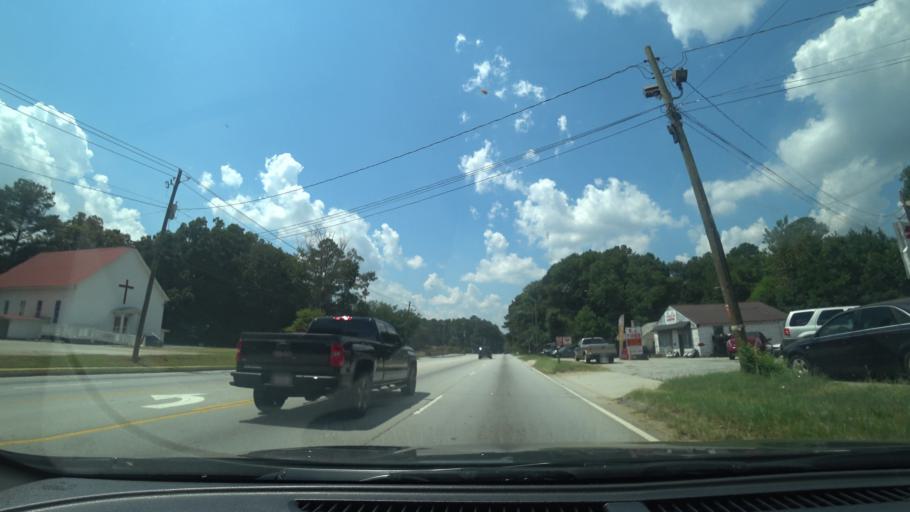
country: US
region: Georgia
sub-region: DeKalb County
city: Redan
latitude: 33.7238
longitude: -84.1743
